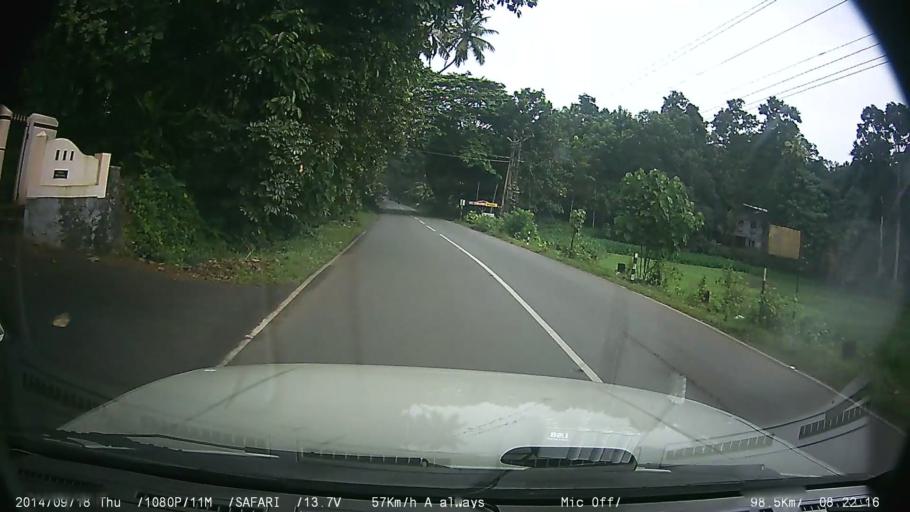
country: IN
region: Kerala
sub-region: Kottayam
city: Palackattumala
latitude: 9.6599
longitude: 76.6117
